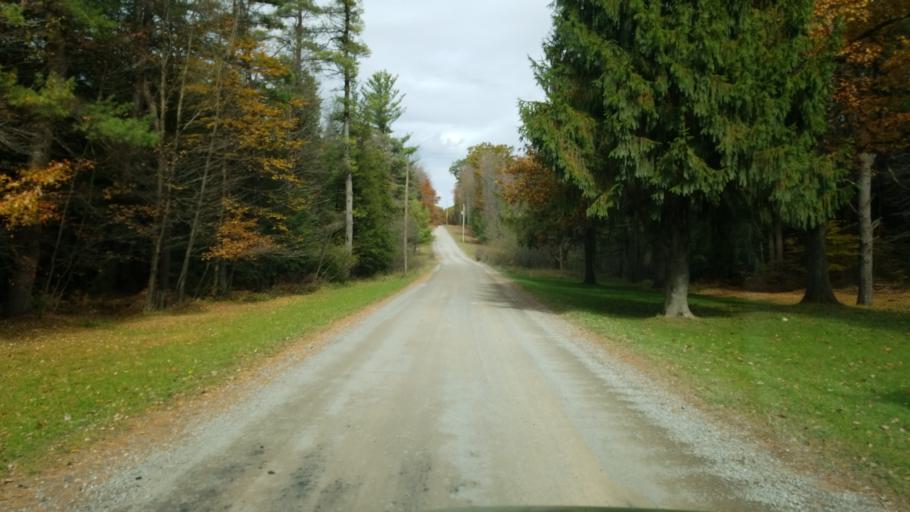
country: US
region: Pennsylvania
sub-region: Clearfield County
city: Clearfield
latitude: 41.1796
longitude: -78.4434
